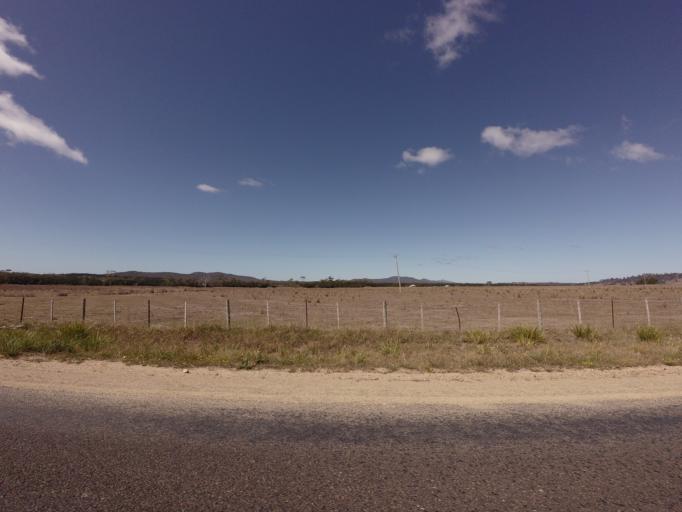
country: AU
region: Tasmania
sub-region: Break O'Day
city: St Helens
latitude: -41.9474
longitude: 148.2022
